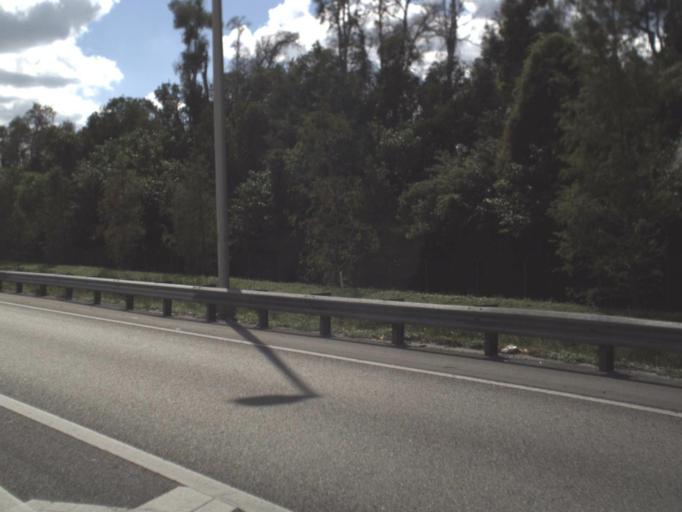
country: US
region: Florida
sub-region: Broward County
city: Davie
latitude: 26.0603
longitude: -80.2154
